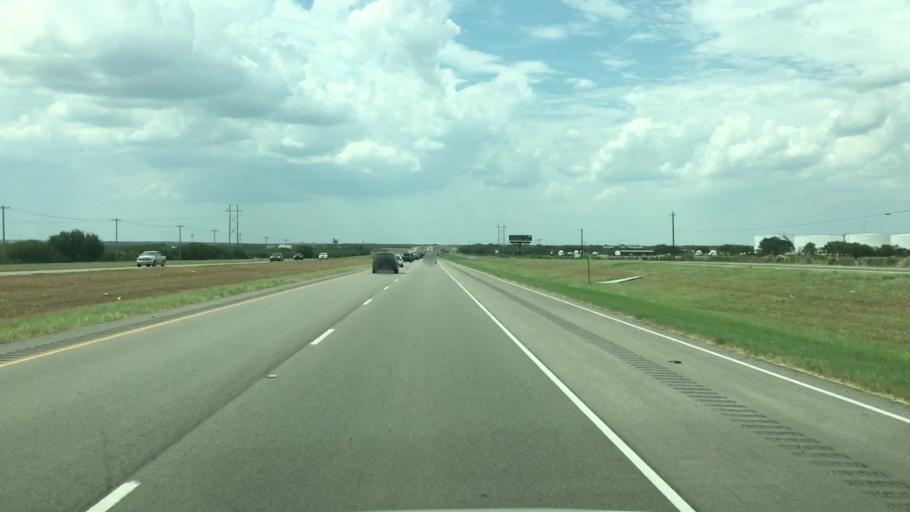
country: US
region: Texas
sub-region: Live Oak County
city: Three Rivers
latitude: 28.5101
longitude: -98.1677
